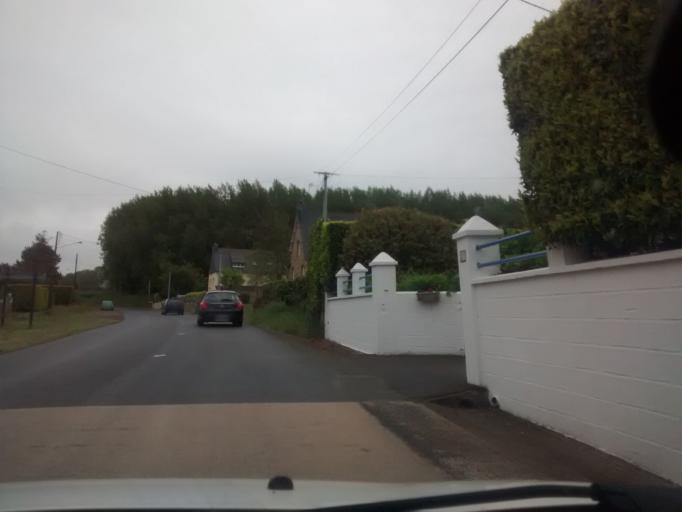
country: FR
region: Brittany
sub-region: Departement des Cotes-d'Armor
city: Penvenan
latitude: 48.8224
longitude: -3.3006
